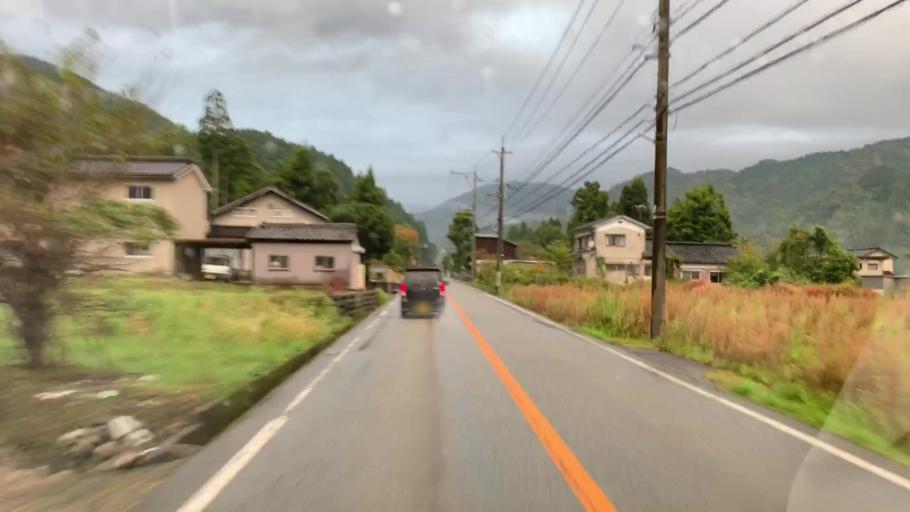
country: JP
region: Toyama
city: Kamiichi
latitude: 36.5841
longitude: 137.3346
